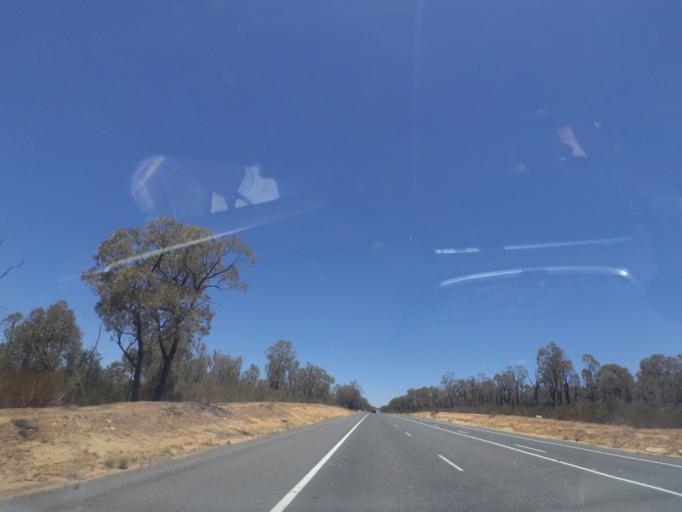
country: AU
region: New South Wales
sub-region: Warrumbungle Shire
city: Coonabarabran
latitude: -30.9015
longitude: 149.4391
